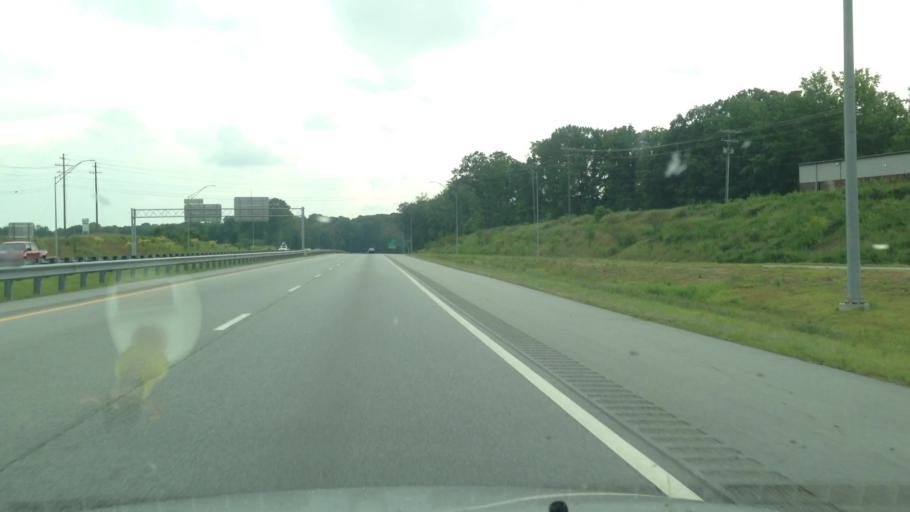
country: US
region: North Carolina
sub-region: Forsyth County
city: Kernersville
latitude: 36.1071
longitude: -80.0485
